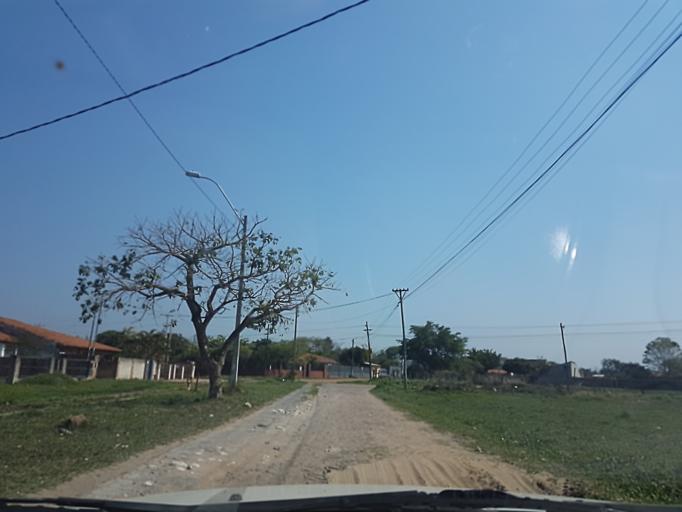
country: PY
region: Central
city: Colonia Mariano Roque Alonso
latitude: -25.2060
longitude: -57.5338
